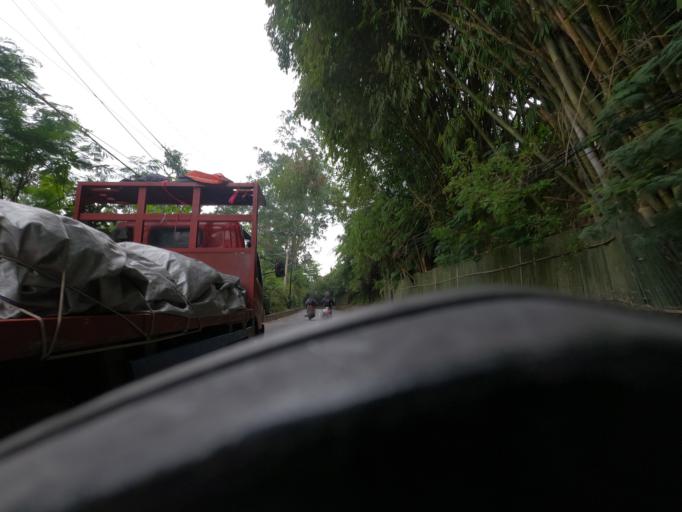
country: ID
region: West Java
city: Lembang
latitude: -6.7984
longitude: 107.5773
